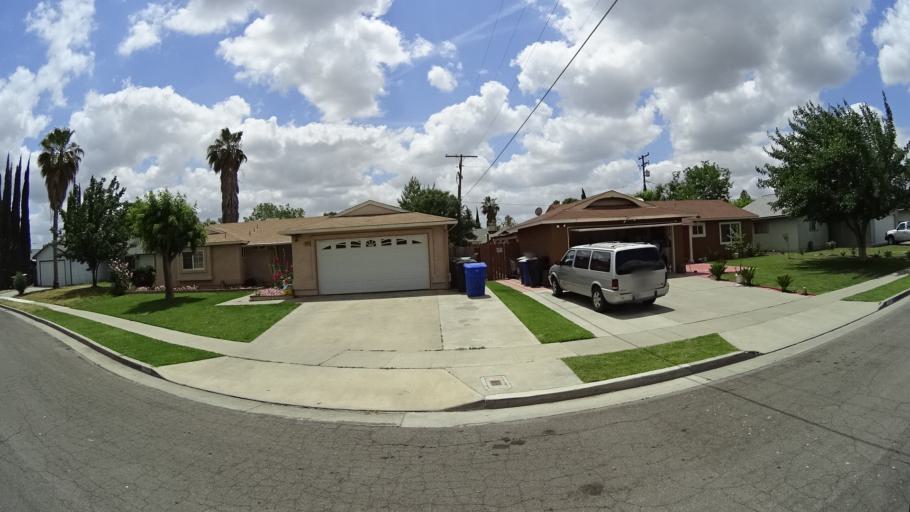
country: US
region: California
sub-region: Kings County
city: Hanford
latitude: 36.3116
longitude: -119.6702
